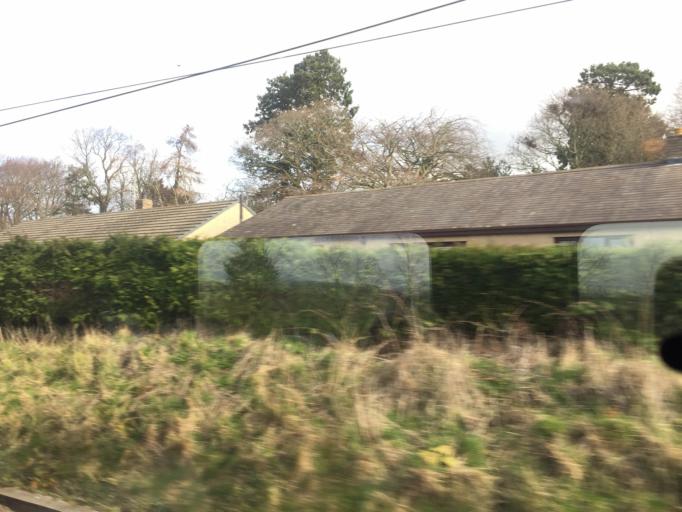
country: GB
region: England
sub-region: Cumbria
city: Penrith
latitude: 54.6425
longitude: -2.7592
